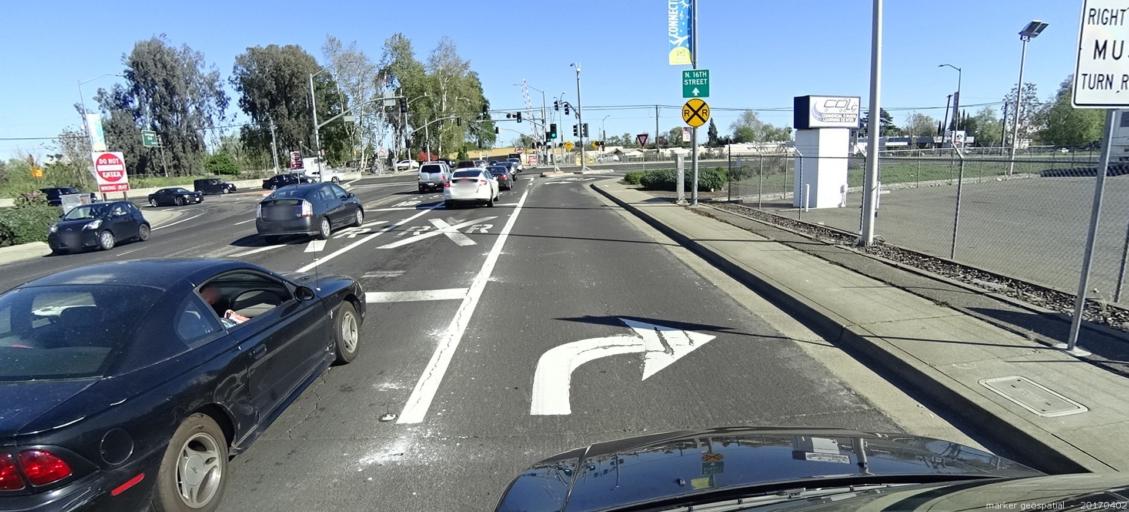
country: US
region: California
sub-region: Sacramento County
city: Sacramento
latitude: 38.5947
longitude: -121.4791
